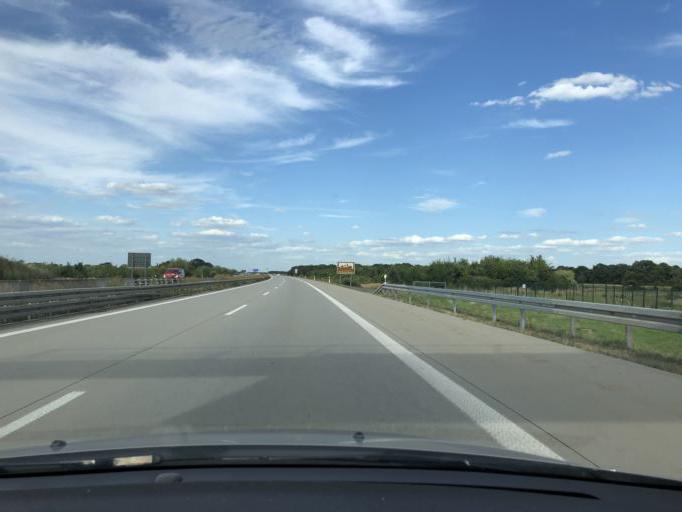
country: DE
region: Saxony
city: Grossposna
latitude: 51.2928
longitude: 12.5298
